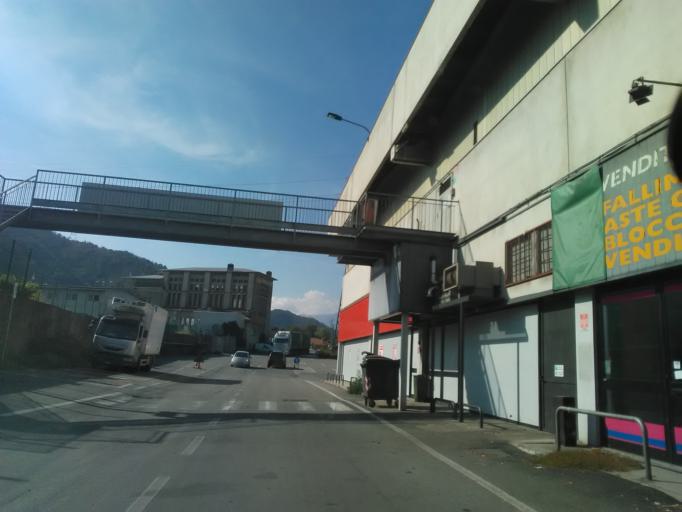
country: IT
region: Piedmont
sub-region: Provincia di Vercelli
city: Serravalle Sesia
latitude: 45.6986
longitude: 8.2890
